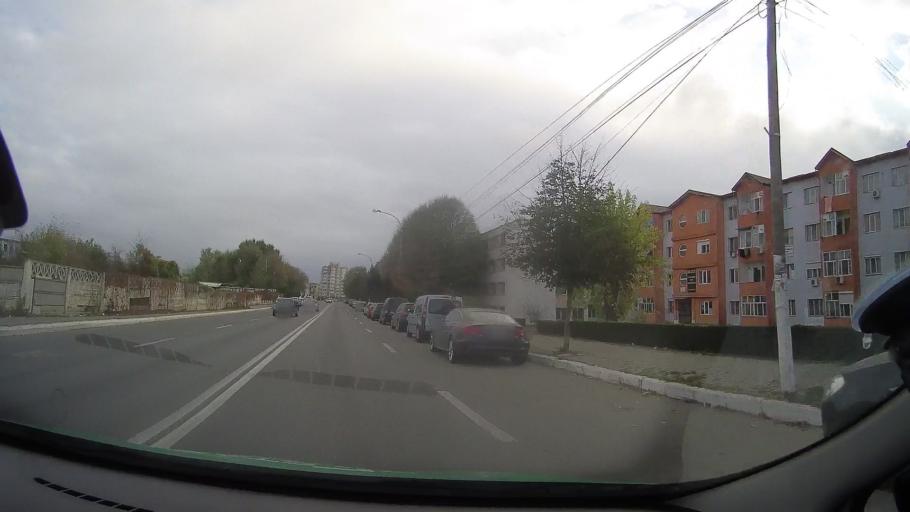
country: RO
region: Constanta
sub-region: Municipiul Medgidia
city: Medgidia
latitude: 44.2644
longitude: 28.2598
